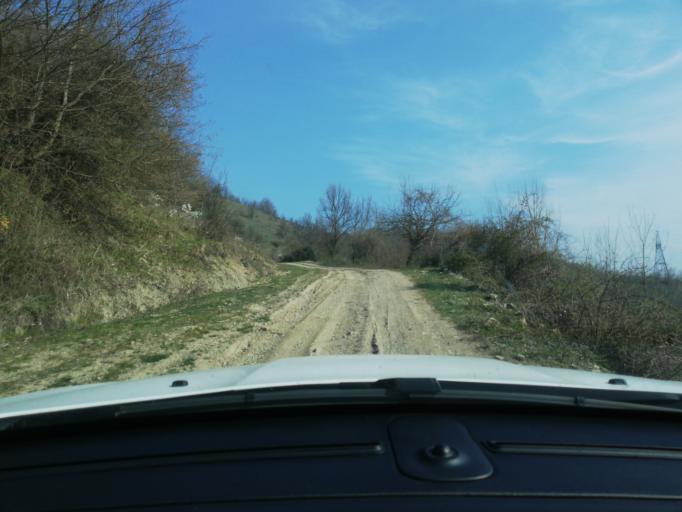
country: TR
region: Karabuk
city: Yenice
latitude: 41.2702
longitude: 32.3564
